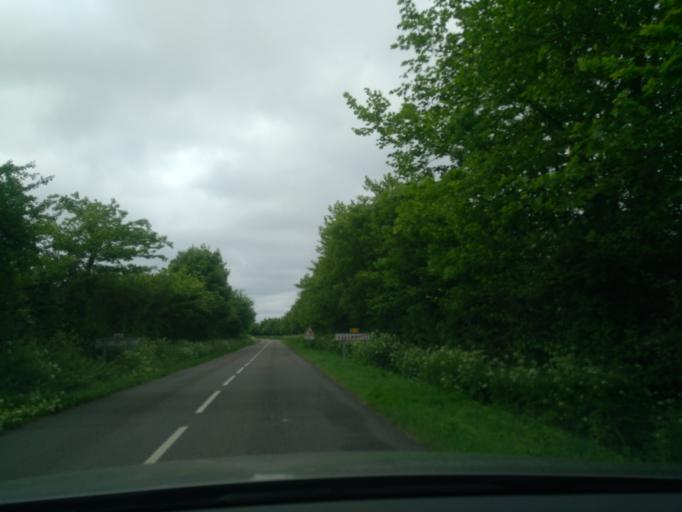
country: FR
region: Lower Normandy
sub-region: Departement de la Manche
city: Sainte-Mere-Eglise
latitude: 49.4580
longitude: -1.2669
